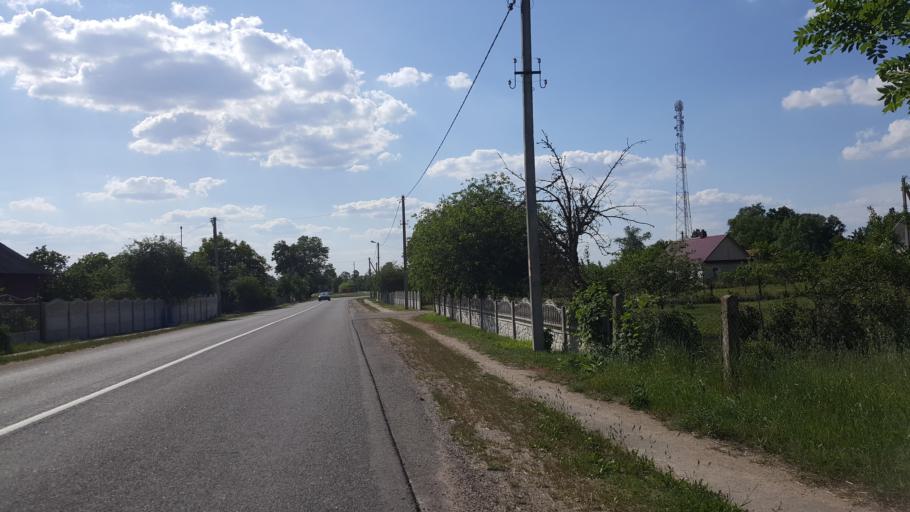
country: BY
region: Brest
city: Kobryn
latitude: 52.3388
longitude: 24.2440
